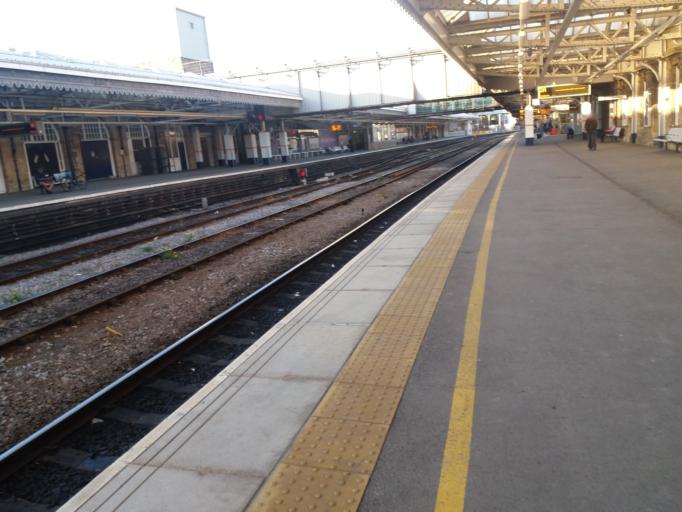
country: GB
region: England
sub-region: Sheffield
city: Sheffield
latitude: 53.3775
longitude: -1.4624
